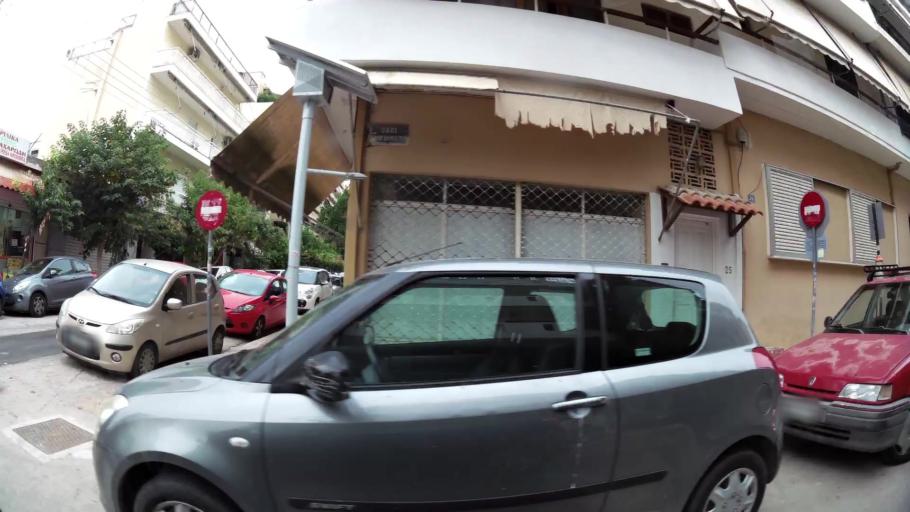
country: GR
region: Attica
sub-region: Nomarchia Athinas
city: Nea Ionia
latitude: 38.0399
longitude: 23.7645
